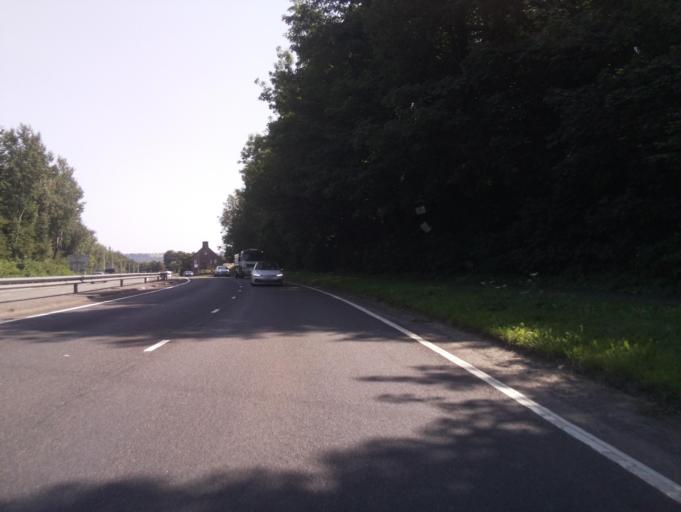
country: GB
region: Wales
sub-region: Caerphilly County Borough
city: Llanbradach
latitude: 51.5955
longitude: -3.2304
